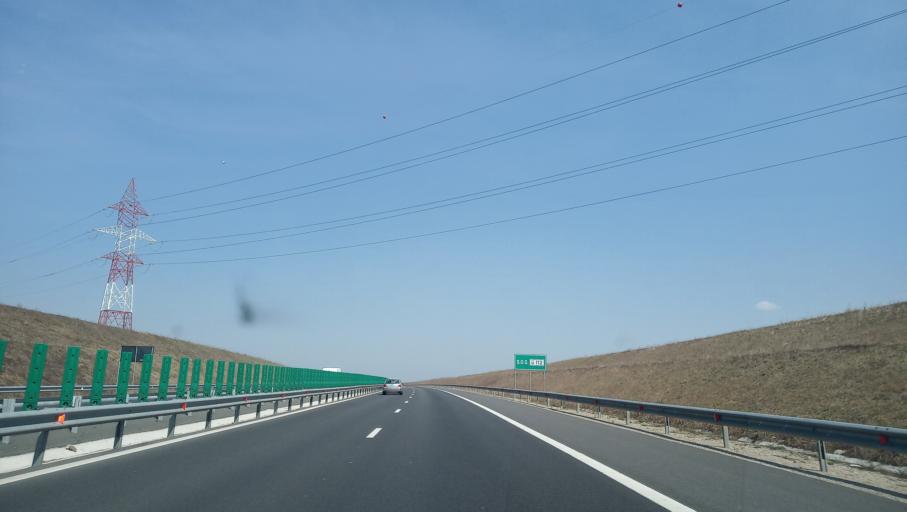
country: RO
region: Alba
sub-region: Comuna Unirea
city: Unirea
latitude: 46.3931
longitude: 23.7864
